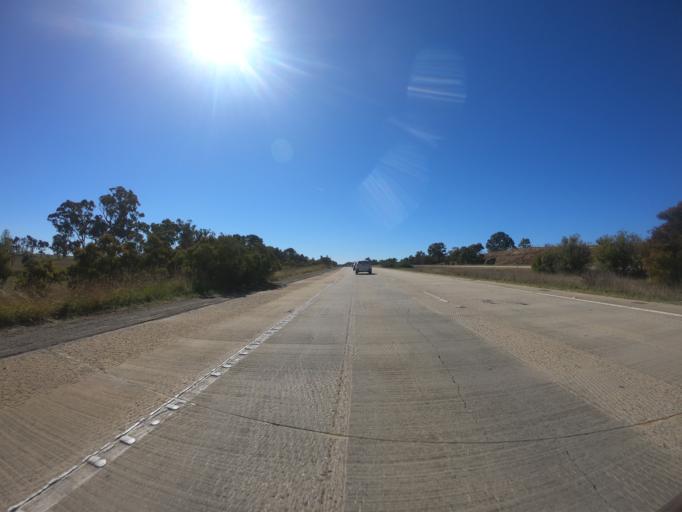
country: AU
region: New South Wales
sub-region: Yass Valley
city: Gundaroo
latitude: -35.1380
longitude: 149.3377
